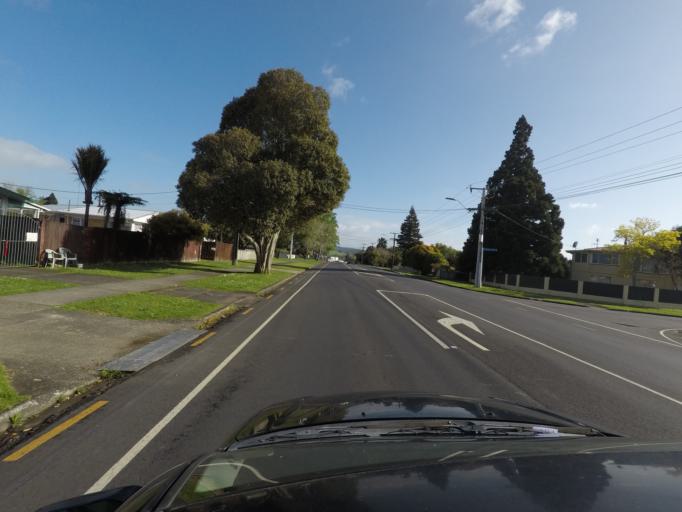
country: NZ
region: Northland
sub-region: Whangarei
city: Whangarei
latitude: -35.6890
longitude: 174.3270
